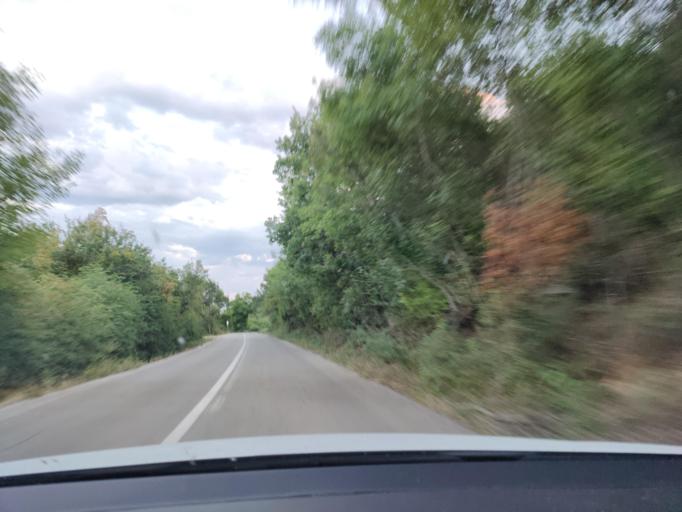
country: GR
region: Central Macedonia
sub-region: Nomos Serron
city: Chrysochorafa
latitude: 41.1647
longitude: 23.1823
